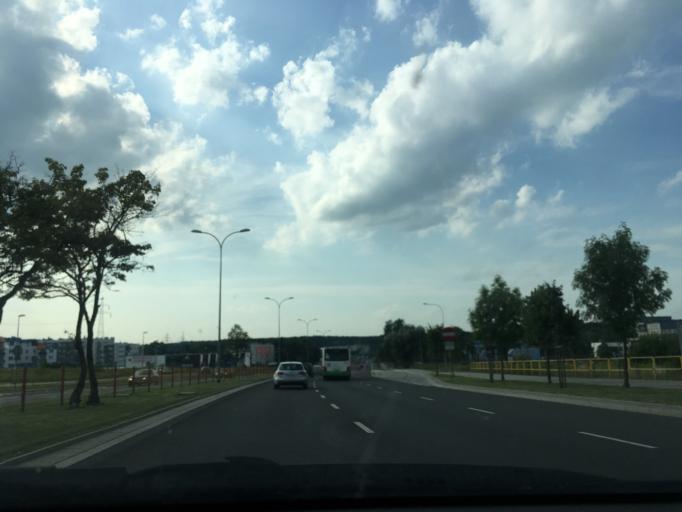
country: PL
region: Podlasie
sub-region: Bialystok
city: Bialystok
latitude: 53.1547
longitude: 23.1598
